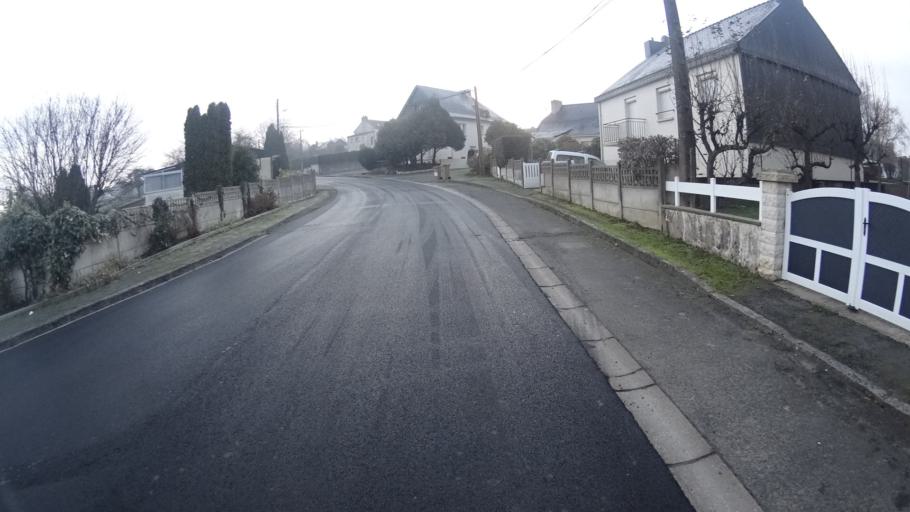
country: FR
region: Pays de la Loire
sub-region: Departement de la Loire-Atlantique
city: Saint-Nicolas-de-Redon
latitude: 47.6452
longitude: -2.0679
